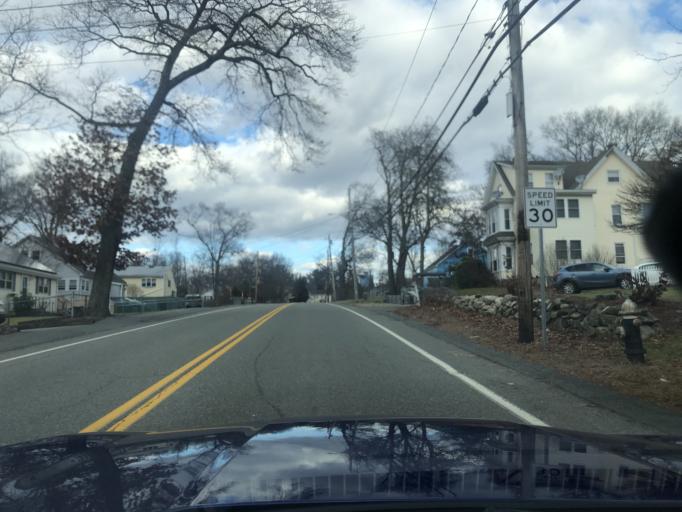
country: US
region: Massachusetts
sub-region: Plymouth County
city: Brockton
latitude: 42.1020
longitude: -71.0073
